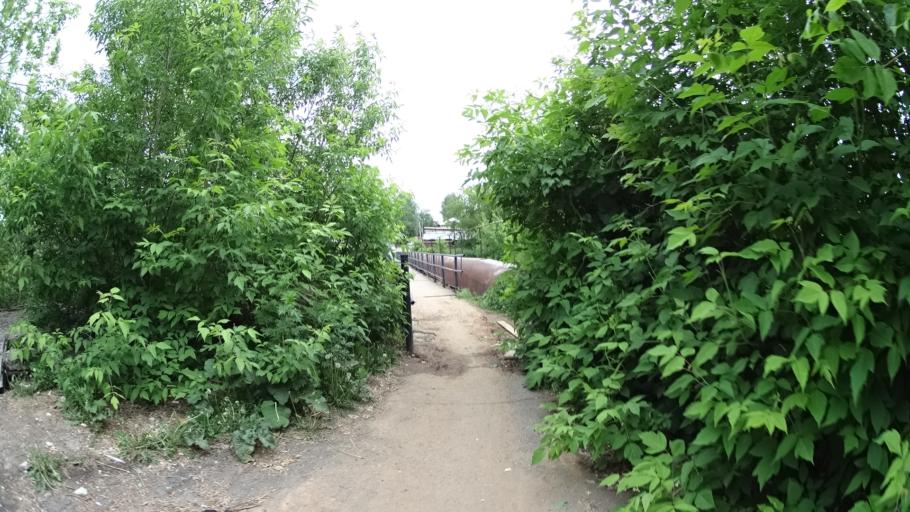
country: RU
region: Perm
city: Perm
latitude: 58.0193
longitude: 56.2643
